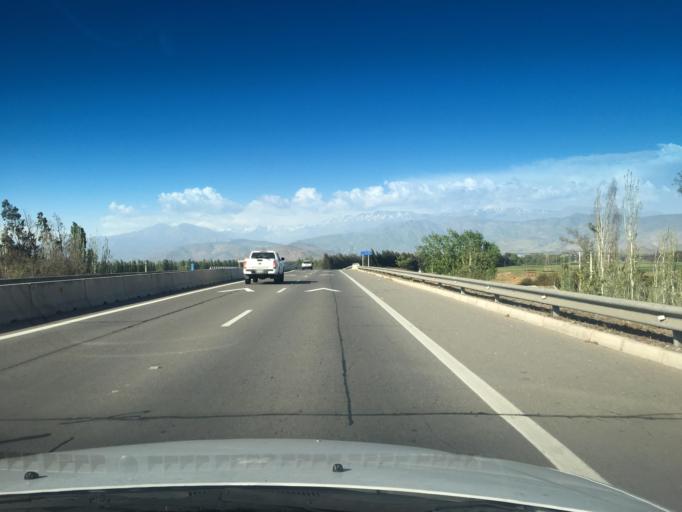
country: CL
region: Santiago Metropolitan
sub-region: Provincia de Chacabuco
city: Chicureo Abajo
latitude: -33.2971
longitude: -70.7240
